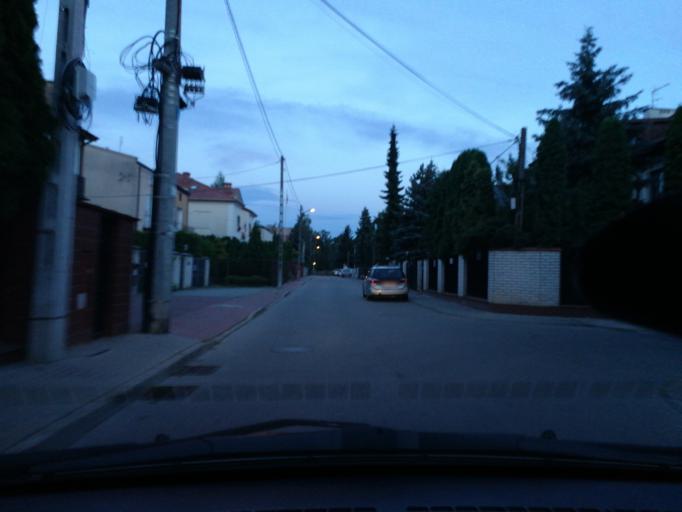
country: PL
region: Masovian Voivodeship
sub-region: Warszawa
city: Wilanow
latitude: 52.1700
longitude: 21.0805
